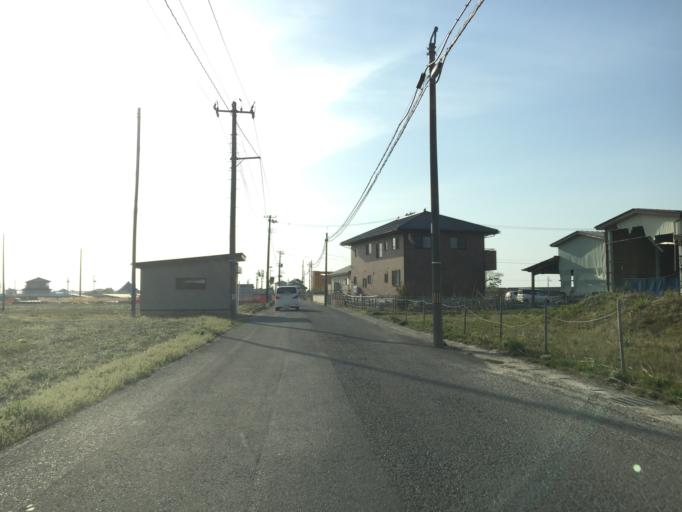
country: JP
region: Miyagi
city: Watari
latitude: 38.0277
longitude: 140.8957
